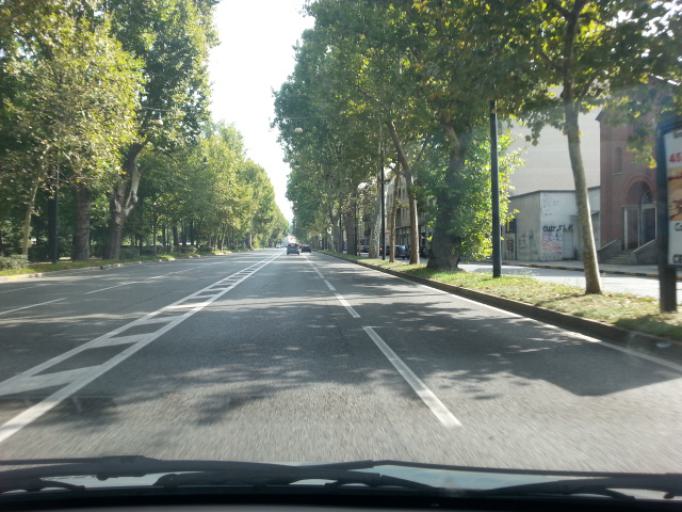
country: IT
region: Piedmont
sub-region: Provincia di Torino
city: Turin
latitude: 45.0649
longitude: 7.7029
